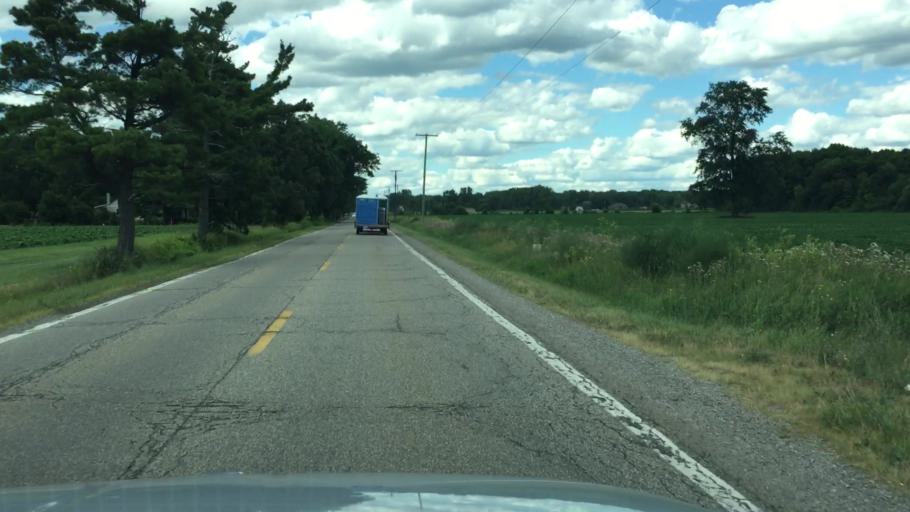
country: US
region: Michigan
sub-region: Macomb County
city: Armada
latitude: 42.8553
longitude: -82.9445
